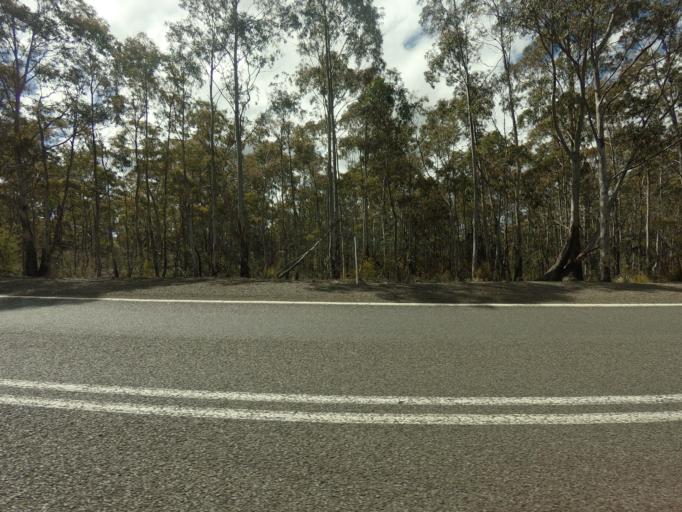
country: AU
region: Tasmania
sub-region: Break O'Day
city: St Helens
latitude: -42.0102
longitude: 147.9049
